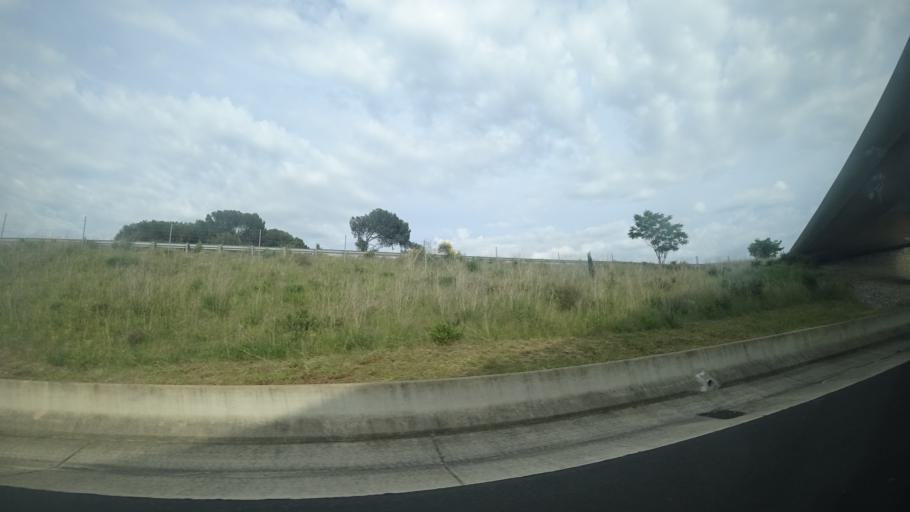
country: FR
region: Languedoc-Roussillon
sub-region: Departement de l'Herault
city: Aspiran
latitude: 43.5716
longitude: 3.4643
